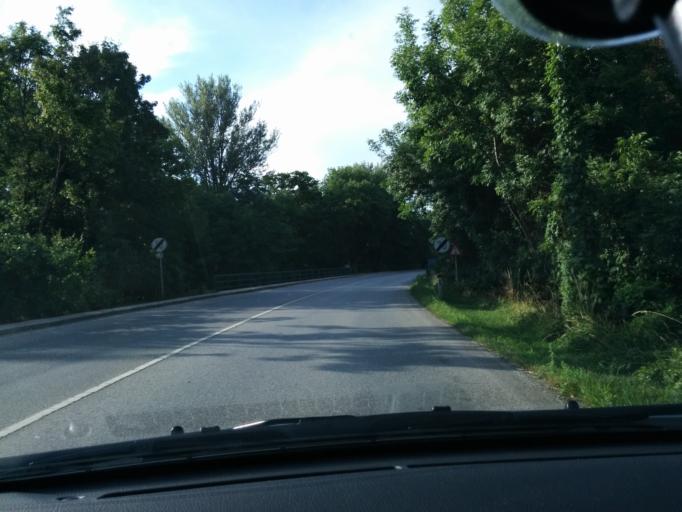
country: AT
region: Lower Austria
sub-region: Politischer Bezirk Baden
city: Gunselsdorf
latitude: 47.9424
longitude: 16.2602
